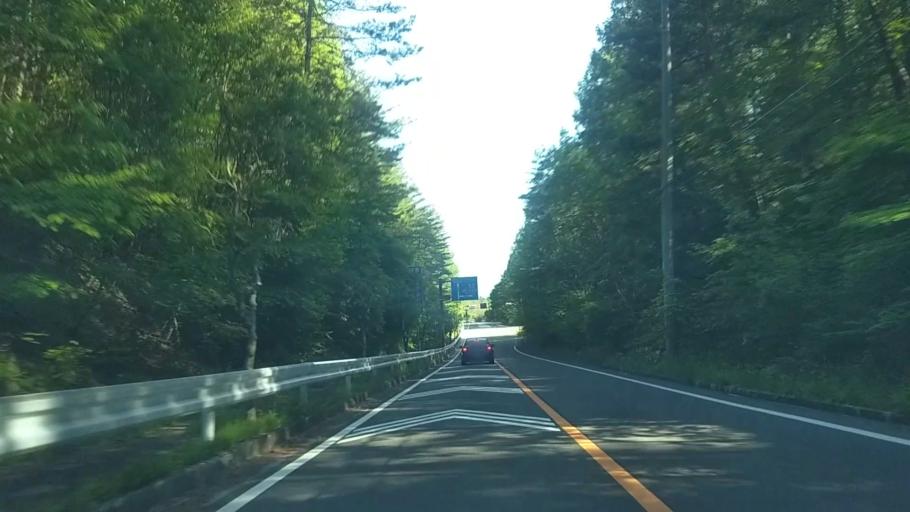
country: JP
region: Nagano
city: Chino
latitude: 35.8957
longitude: 138.3255
